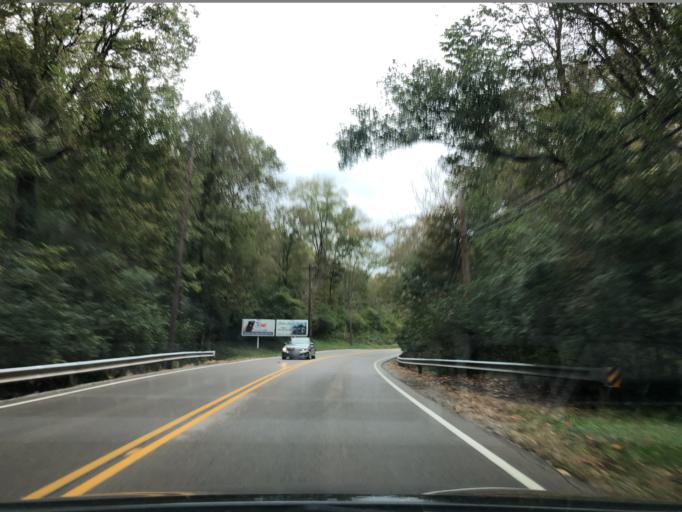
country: US
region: Ohio
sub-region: Hamilton County
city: Mariemont
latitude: 39.1681
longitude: -84.3780
